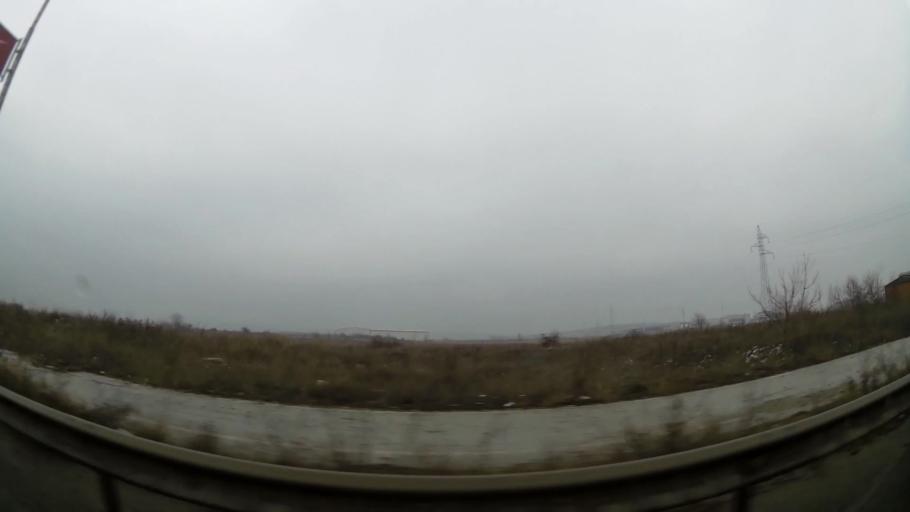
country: MK
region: Suto Orizari
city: Suto Orizare
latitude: 42.0487
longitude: 21.3855
